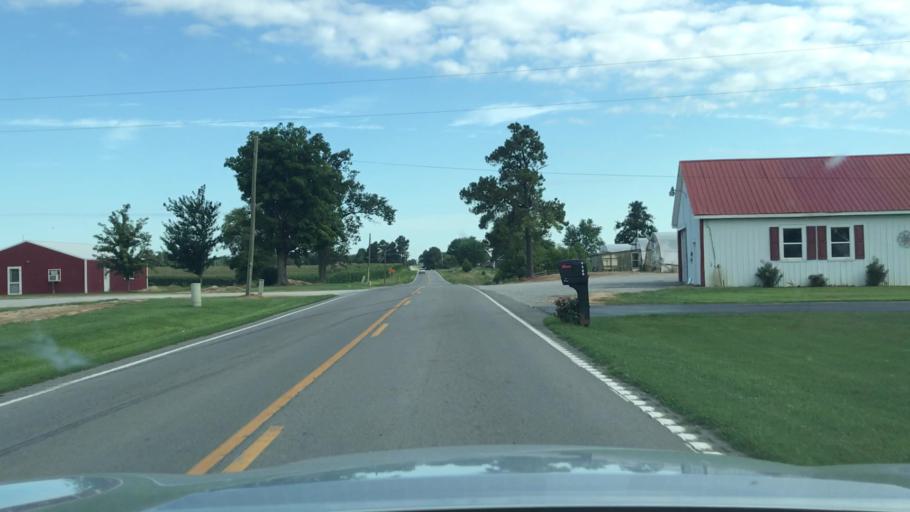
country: US
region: Kentucky
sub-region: Todd County
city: Elkton
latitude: 36.8593
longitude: -87.1594
